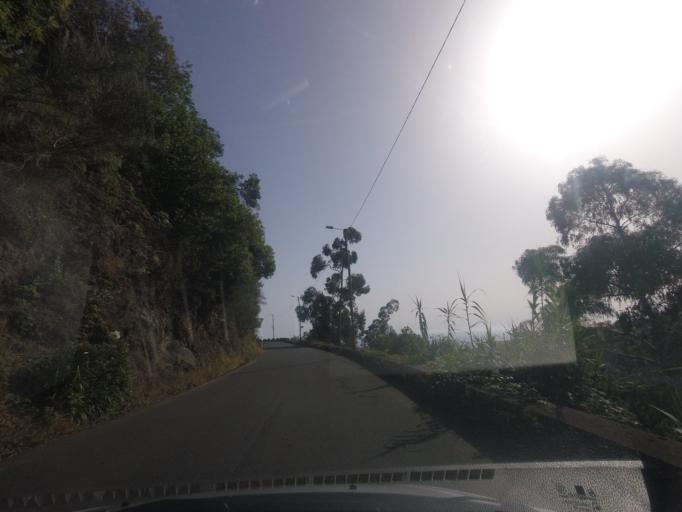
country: PT
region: Madeira
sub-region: Calheta
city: Arco da Calheta
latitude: 32.7296
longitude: -17.1531
